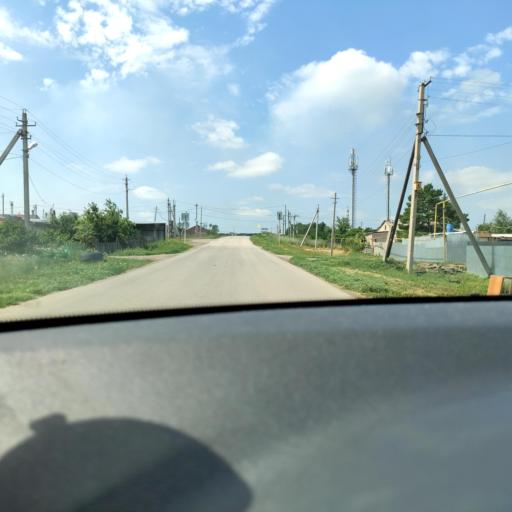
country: RU
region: Samara
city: Kinel'
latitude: 53.3443
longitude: 50.5197
